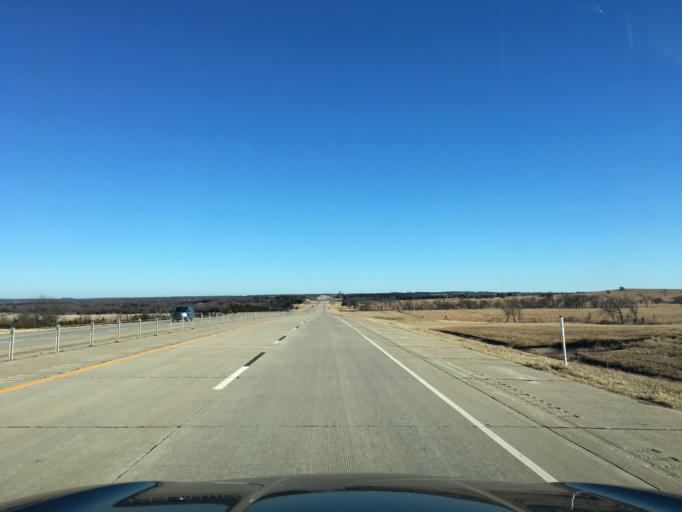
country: US
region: Oklahoma
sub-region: Payne County
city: Yale
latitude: 36.2251
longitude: -96.6381
